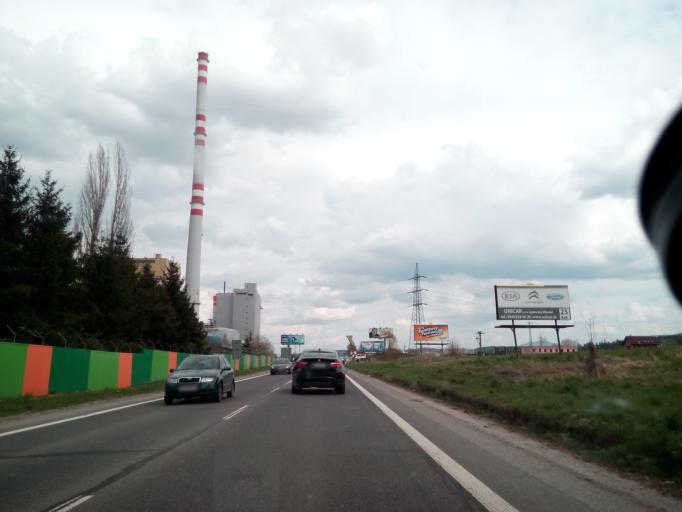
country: SK
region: Zilinsky
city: Ruzomberok
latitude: 49.0783
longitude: 19.3277
